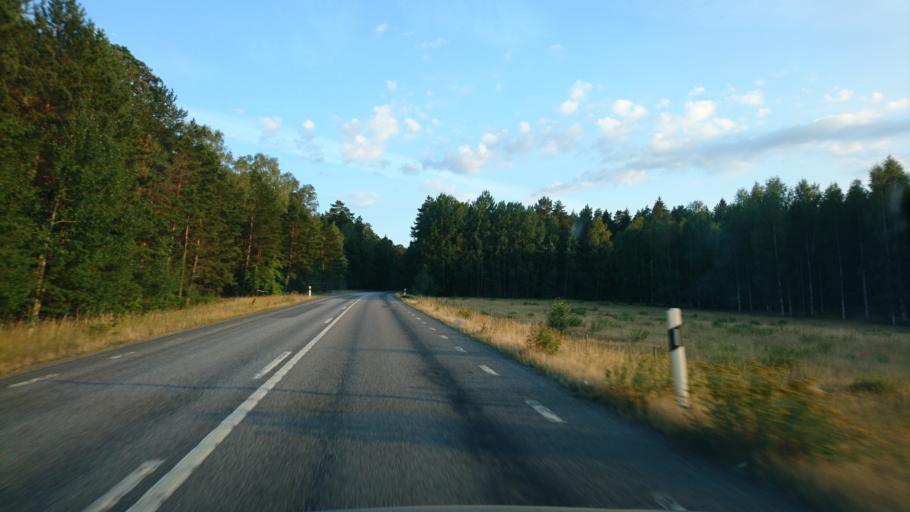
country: SE
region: Uppsala
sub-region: Uppsala Kommun
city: Saevja
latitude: 59.7795
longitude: 17.6636
